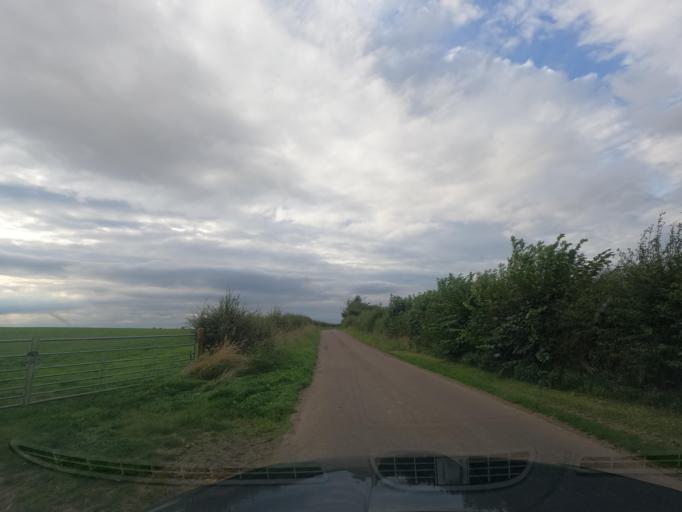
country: GB
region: England
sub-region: Northumberland
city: Ancroft
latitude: 55.7223
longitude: -2.0841
